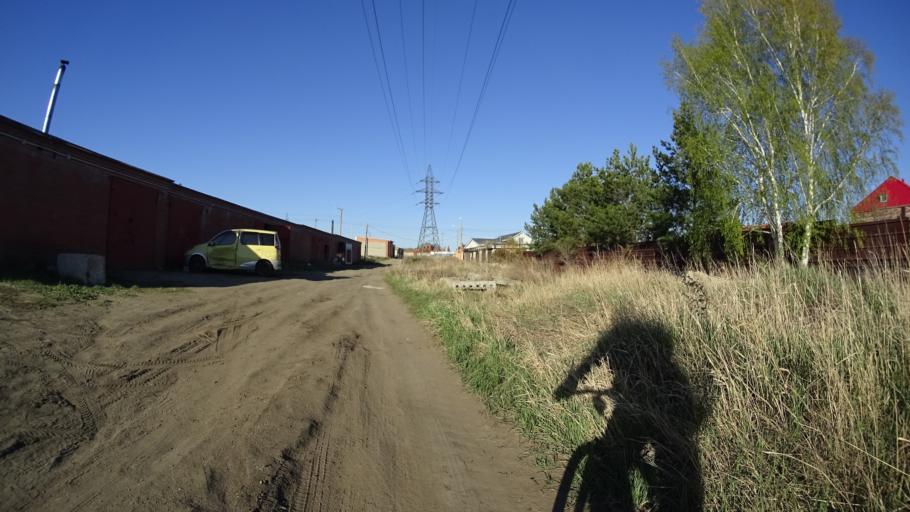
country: RU
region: Chelyabinsk
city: Troitsk
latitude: 54.0706
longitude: 61.5322
